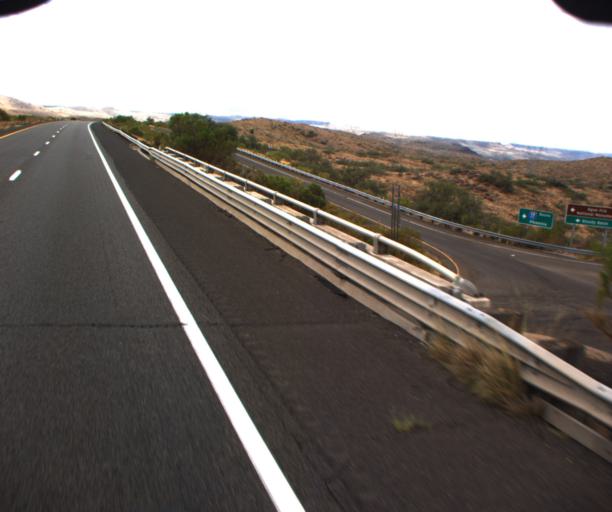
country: US
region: Arizona
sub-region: Yavapai County
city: Cordes Lakes
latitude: 34.2842
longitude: -112.1210
